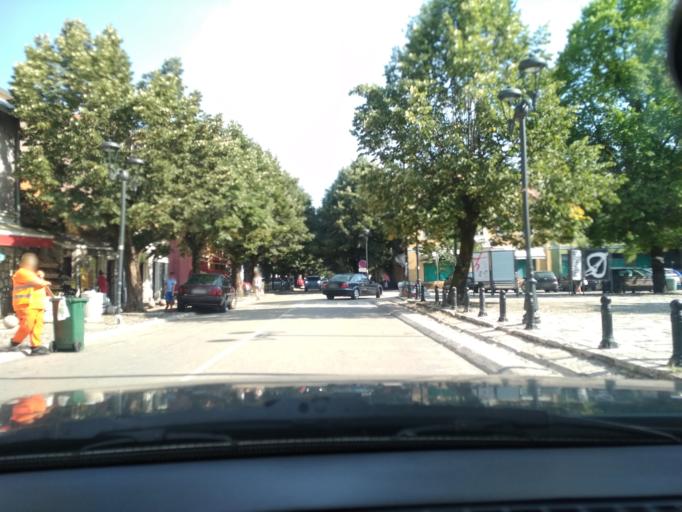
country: ME
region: Cetinje
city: Cetinje
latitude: 42.3898
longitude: 18.9247
